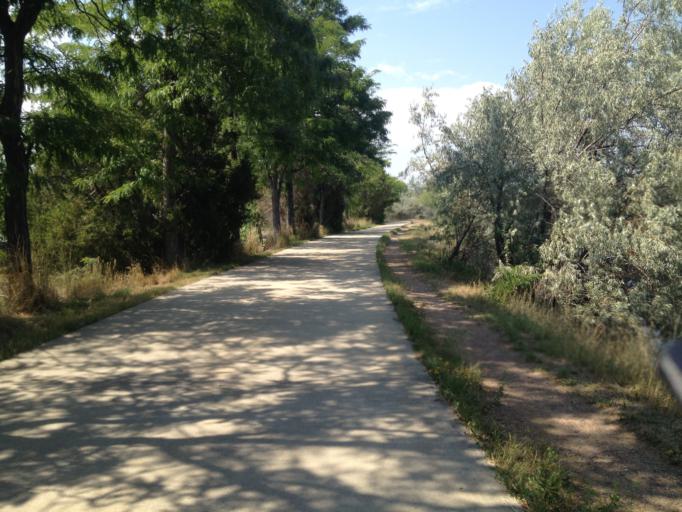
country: US
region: Colorado
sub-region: Boulder County
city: Boulder
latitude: 40.0261
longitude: -105.2183
